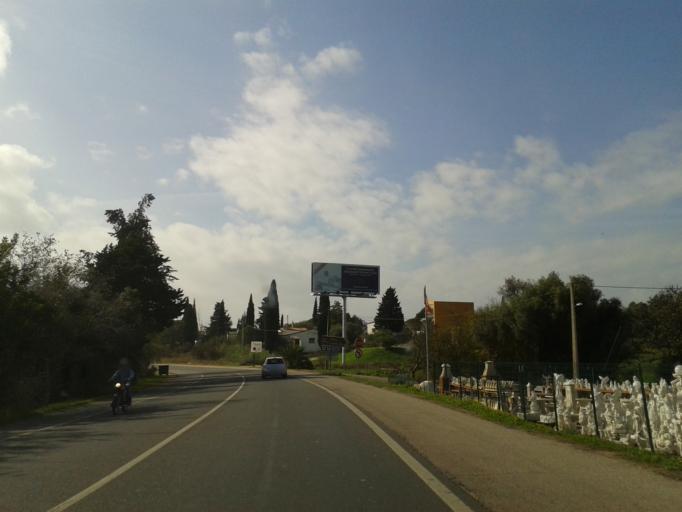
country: PT
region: Faro
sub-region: Tavira
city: Tavira
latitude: 37.1441
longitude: -7.6211
